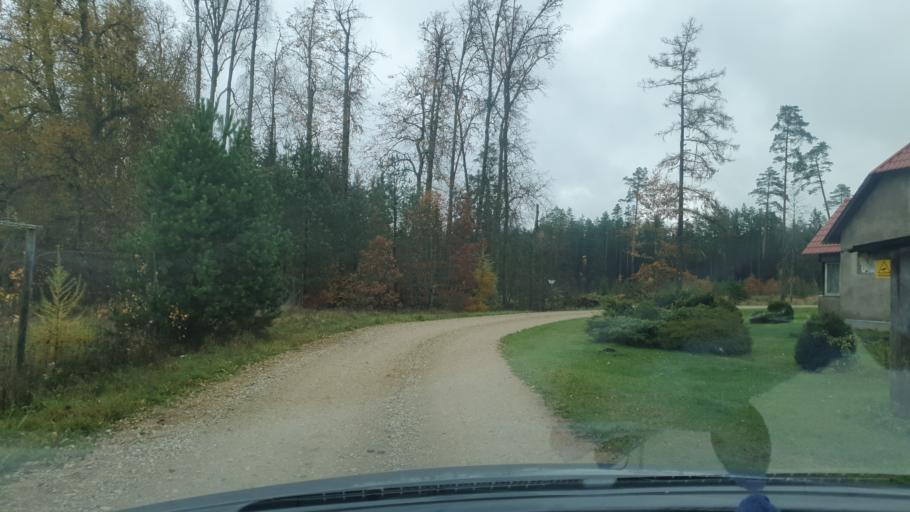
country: EE
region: Viljandimaa
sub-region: Karksi vald
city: Karksi-Nuia
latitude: 57.9919
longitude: 25.6397
